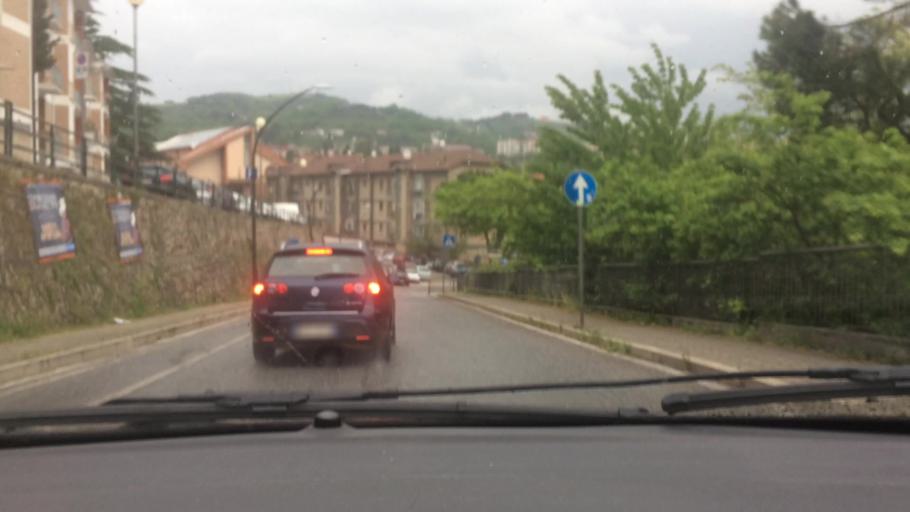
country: IT
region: Basilicate
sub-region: Provincia di Potenza
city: Potenza
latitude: 40.6459
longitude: 15.7965
